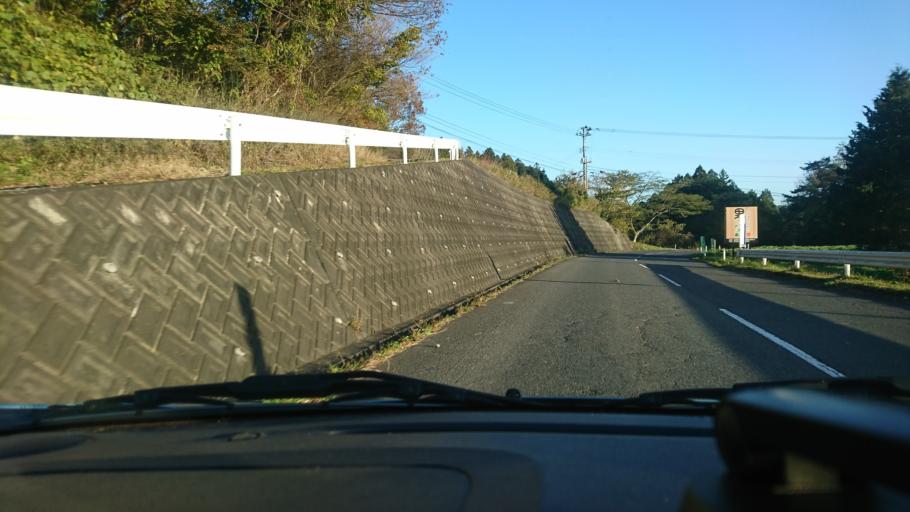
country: JP
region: Iwate
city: Ichinoseki
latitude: 38.8000
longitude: 141.2553
